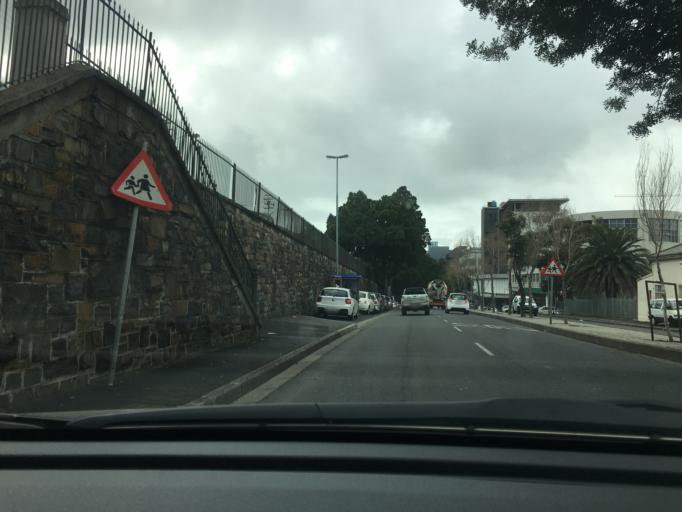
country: ZA
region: Western Cape
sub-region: City of Cape Town
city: Cape Town
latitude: -33.9252
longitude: 18.4123
